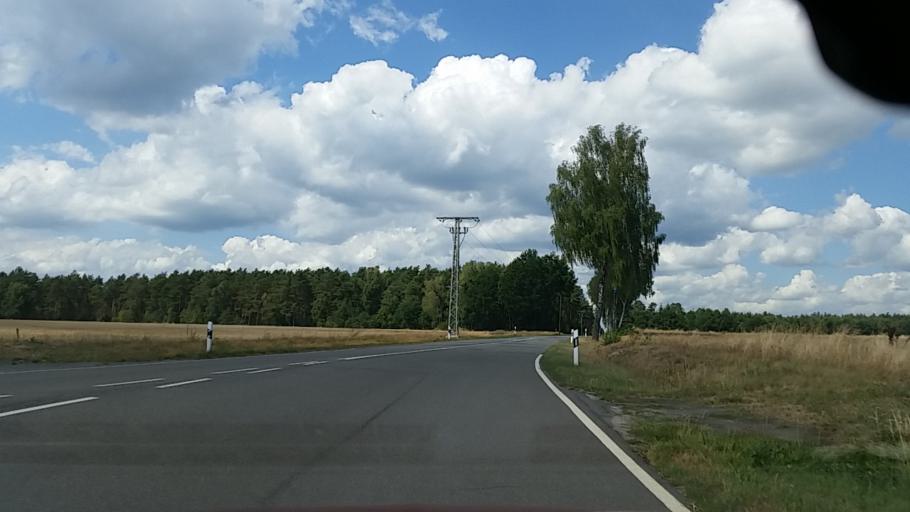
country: DE
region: Lower Saxony
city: Dedelstorf
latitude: 52.7095
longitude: 10.5325
